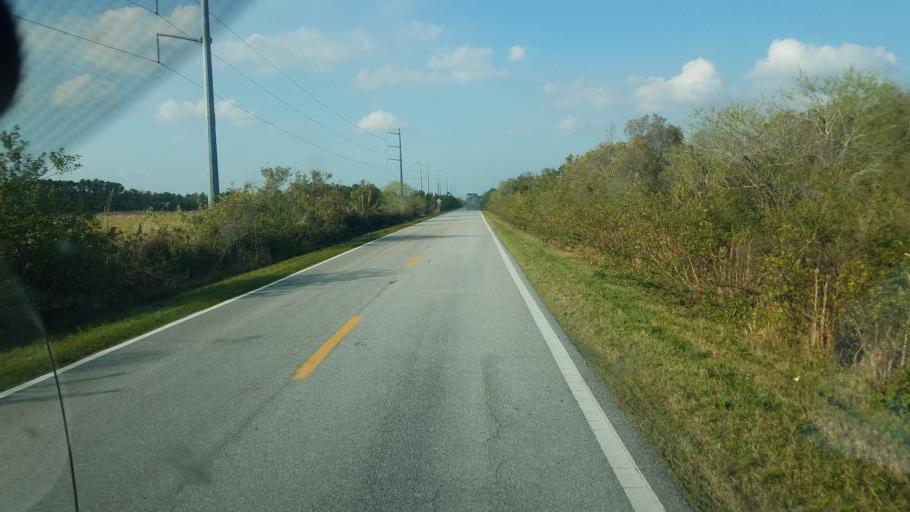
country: US
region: Florida
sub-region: Hardee County
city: Bowling Green
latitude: 27.6675
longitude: -81.9527
